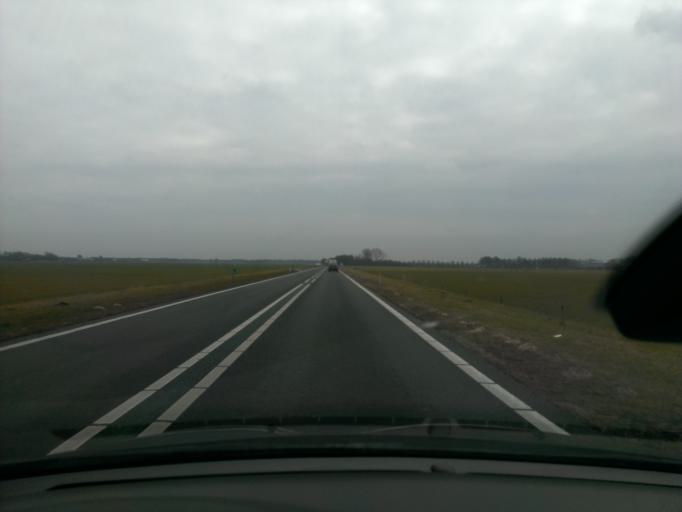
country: NL
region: Overijssel
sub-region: Gemeente Twenterand
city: Vroomshoop
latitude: 52.4940
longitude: 6.5890
